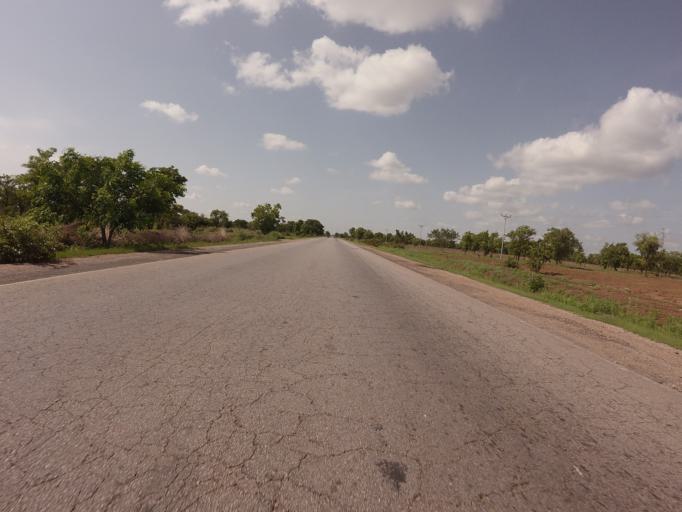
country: GH
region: Northern
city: Savelugu
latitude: 9.9628
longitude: -0.8318
